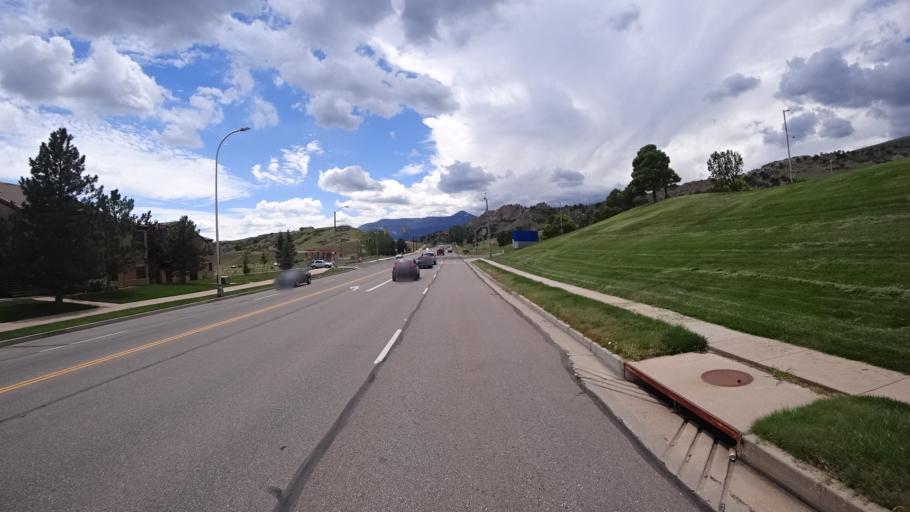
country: US
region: Colorado
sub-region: El Paso County
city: Manitou Springs
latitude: 38.8985
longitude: -104.8717
